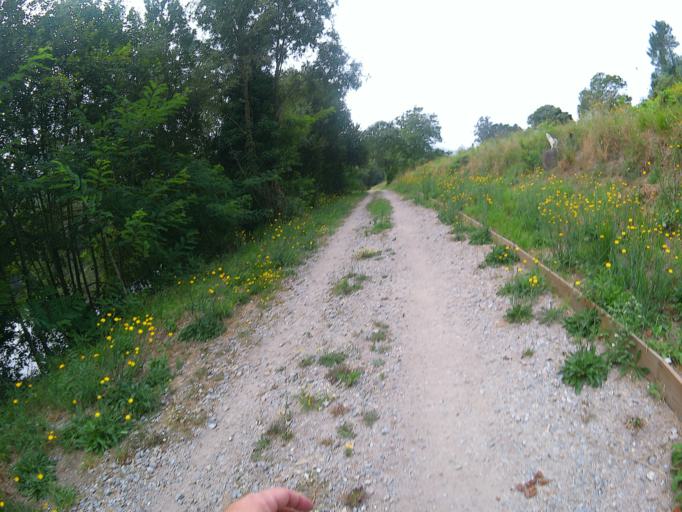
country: PT
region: Viana do Castelo
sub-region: Ponte de Lima
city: Ponte de Lima
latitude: 41.7902
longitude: -8.5149
